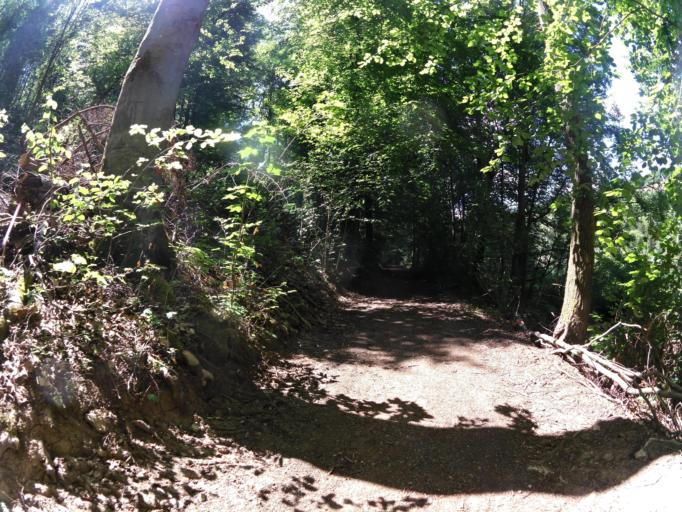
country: DE
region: Bavaria
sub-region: Regierungsbezirk Unterfranken
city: Zellingen
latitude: 49.9038
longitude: 9.8400
